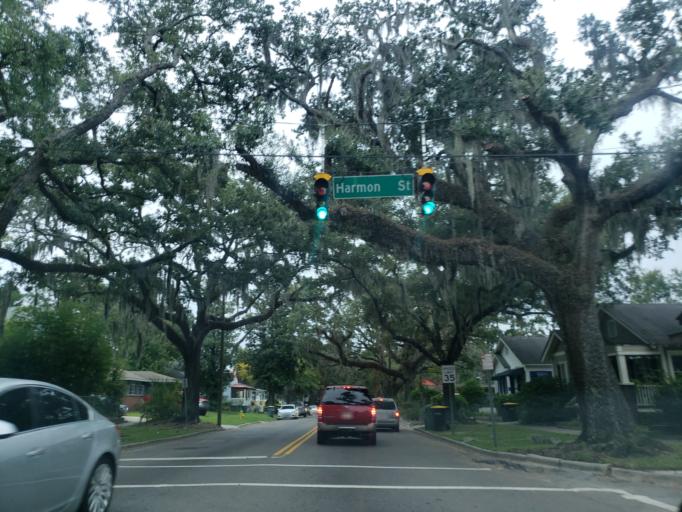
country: US
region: Georgia
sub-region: Chatham County
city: Savannah
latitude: 32.0534
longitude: -81.0861
